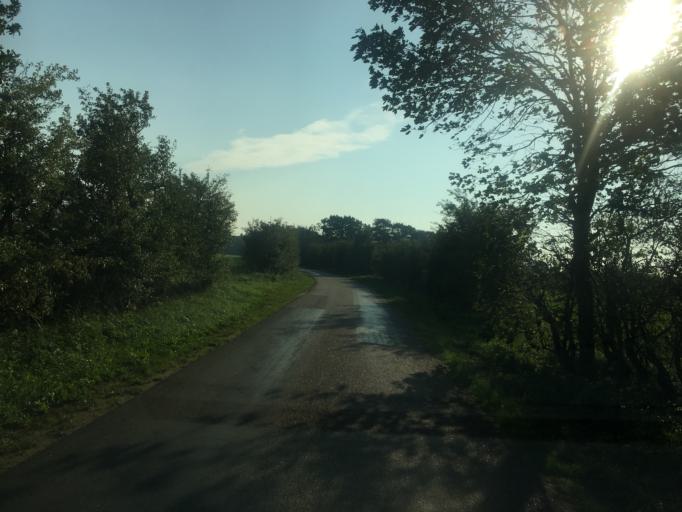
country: DE
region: Schleswig-Holstein
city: Bramstedtlund
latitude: 54.9296
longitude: 9.0613
